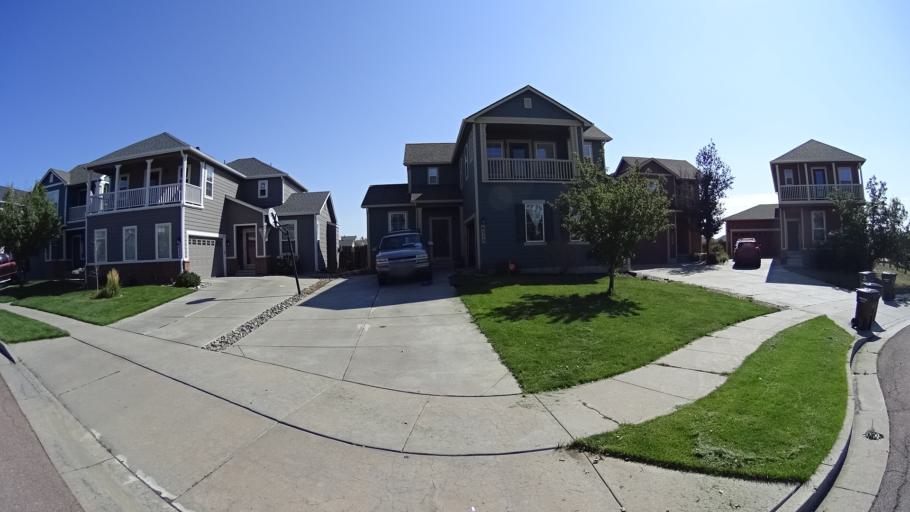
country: US
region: Colorado
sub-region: El Paso County
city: Cimarron Hills
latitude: 38.9269
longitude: -104.7004
